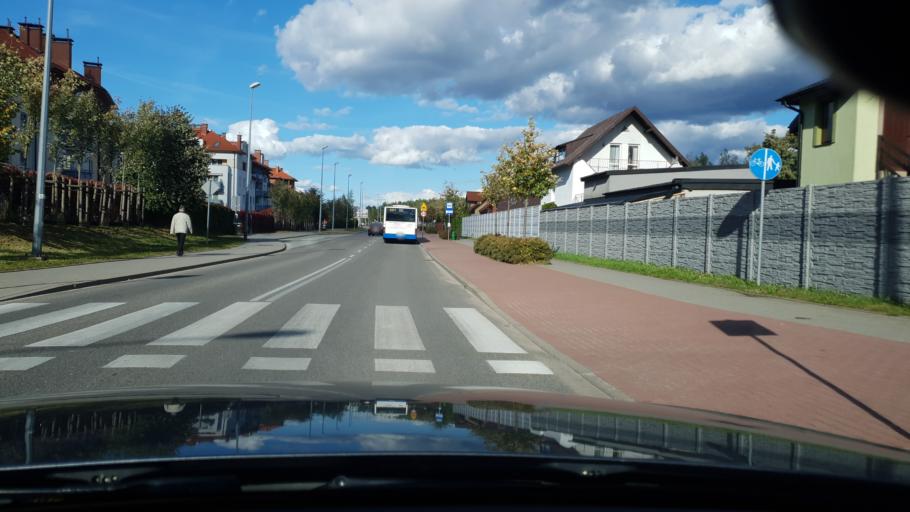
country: PL
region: Pomeranian Voivodeship
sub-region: Powiat kartuski
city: Chwaszczyno
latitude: 54.4950
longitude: 18.4367
